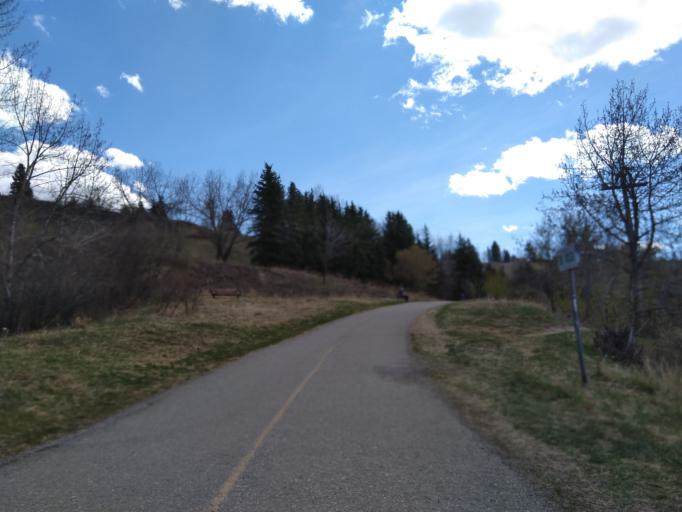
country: CA
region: Alberta
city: Calgary
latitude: 51.0848
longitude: -114.1662
